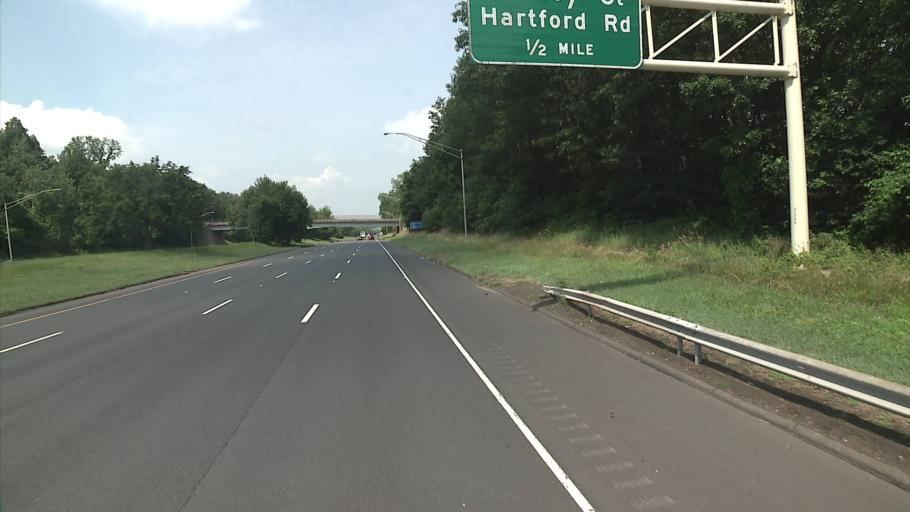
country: US
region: Connecticut
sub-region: Hartford County
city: Manchester
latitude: 41.7630
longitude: -72.5288
